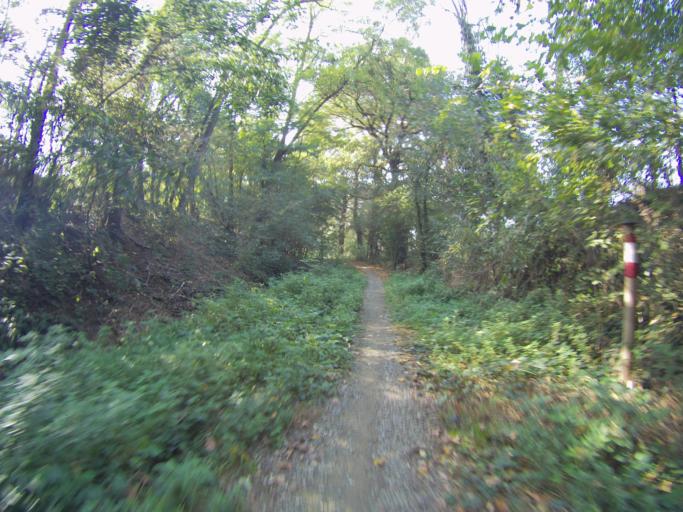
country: IT
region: Emilia-Romagna
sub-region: Provincia di Reggio Emilia
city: Forche
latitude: 44.6651
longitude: 10.5886
